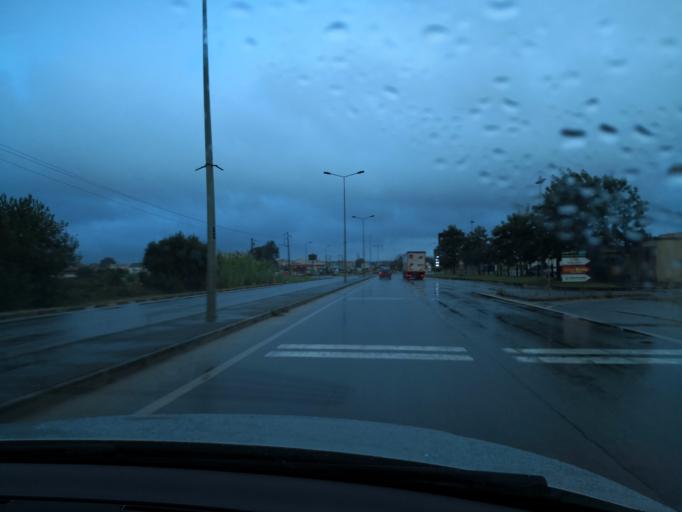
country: PT
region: Setubal
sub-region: Moita
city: Moita
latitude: 38.6500
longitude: -8.9986
